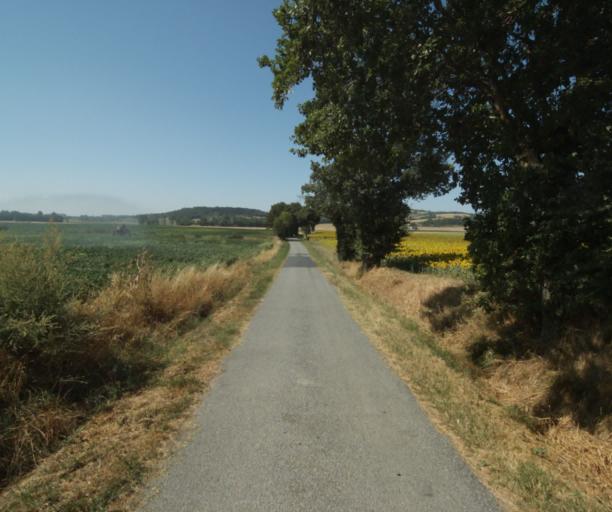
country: FR
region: Midi-Pyrenees
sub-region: Departement du Tarn
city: Puylaurens
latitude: 43.5259
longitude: 1.9584
